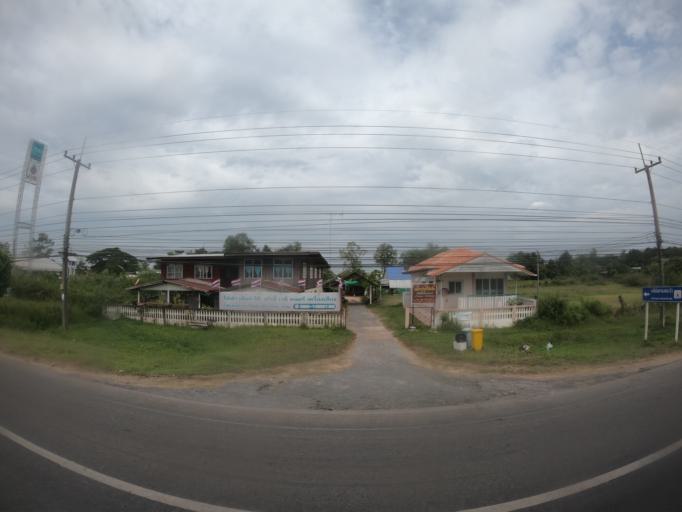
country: TH
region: Roi Et
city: Roi Et
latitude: 16.0654
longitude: 103.6146
